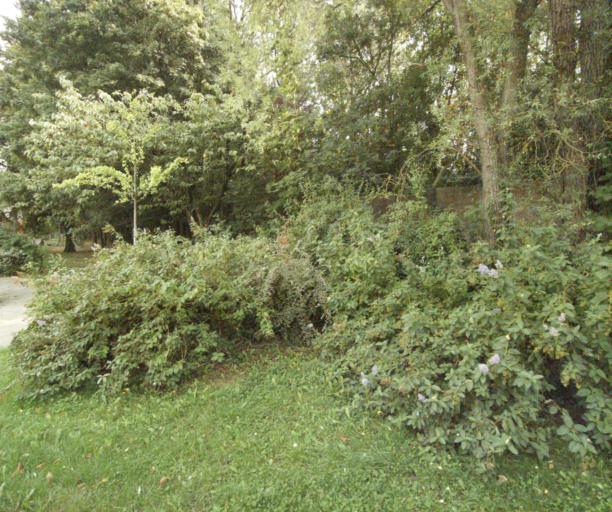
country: FR
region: Nord-Pas-de-Calais
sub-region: Departement du Nord
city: Loos
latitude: 50.6043
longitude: 3.0095
